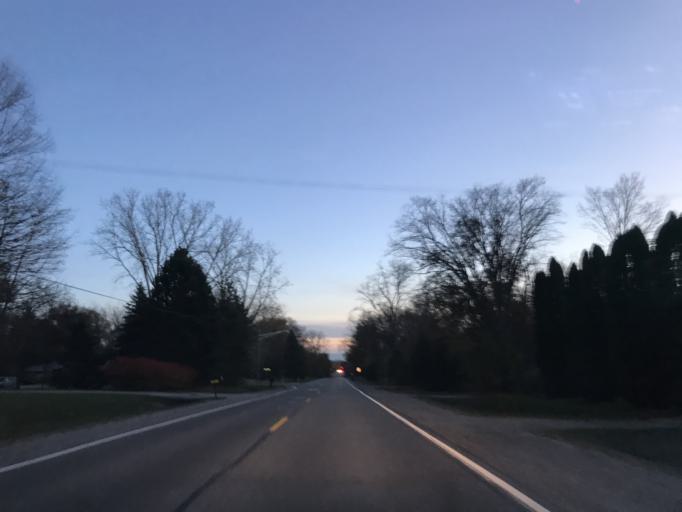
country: US
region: Michigan
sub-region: Oakland County
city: Farmington Hills
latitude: 42.4783
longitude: -83.3674
